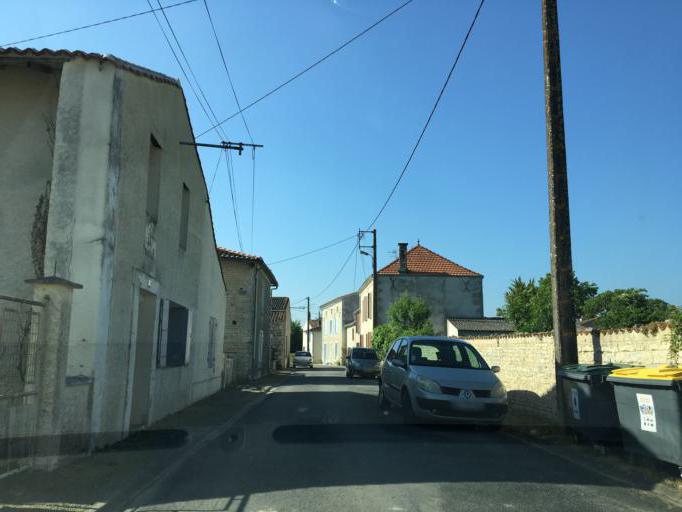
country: FR
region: Poitou-Charentes
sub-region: Departement des Deux-Sevres
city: Beauvoir-sur-Niort
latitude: 46.0961
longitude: -0.5067
